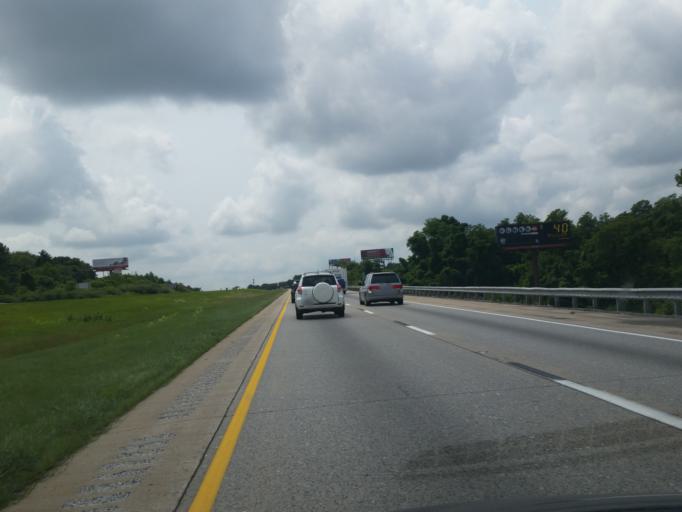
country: US
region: Pennsylvania
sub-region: Dauphin County
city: Linglestown
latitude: 40.3303
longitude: -76.7686
